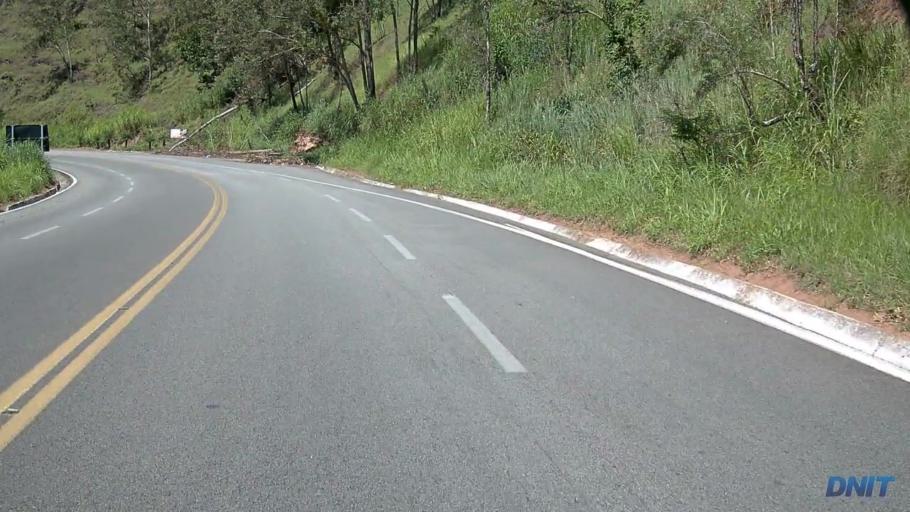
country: BR
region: Minas Gerais
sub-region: Joao Monlevade
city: Joao Monlevade
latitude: -19.8441
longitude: -43.1028
